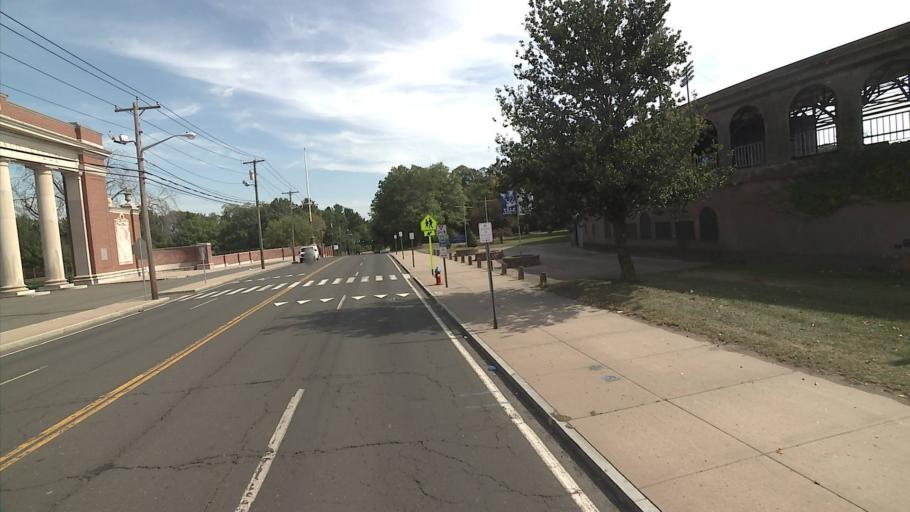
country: US
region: Connecticut
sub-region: New Haven County
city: New Haven
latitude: 41.3100
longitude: -72.9599
